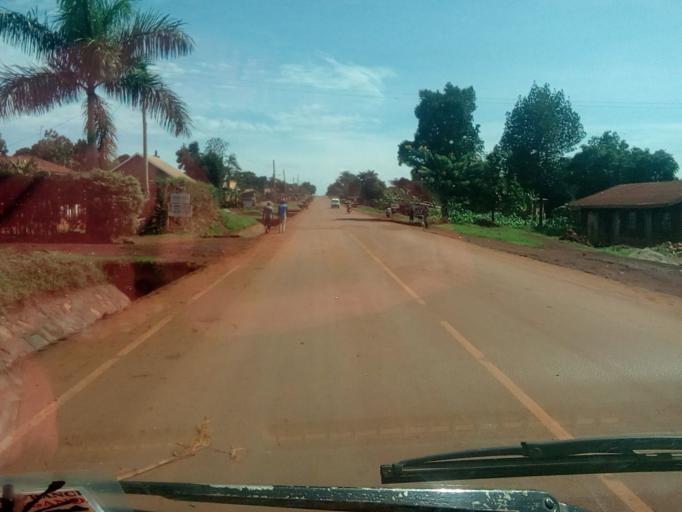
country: UG
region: Eastern Region
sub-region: Jinja District
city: Bugembe
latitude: 0.4939
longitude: 33.2220
